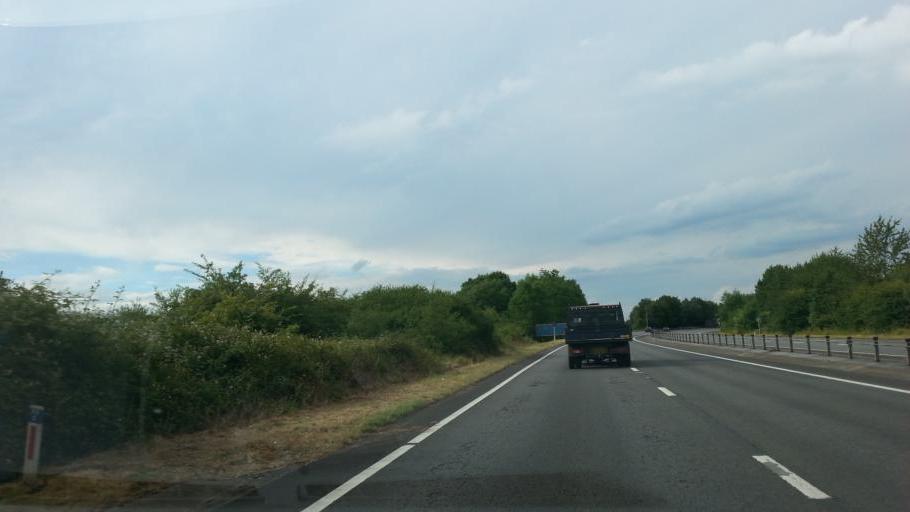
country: GB
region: Wales
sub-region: Monmouthshire
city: Llangwm
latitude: 51.7577
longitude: -2.8426
